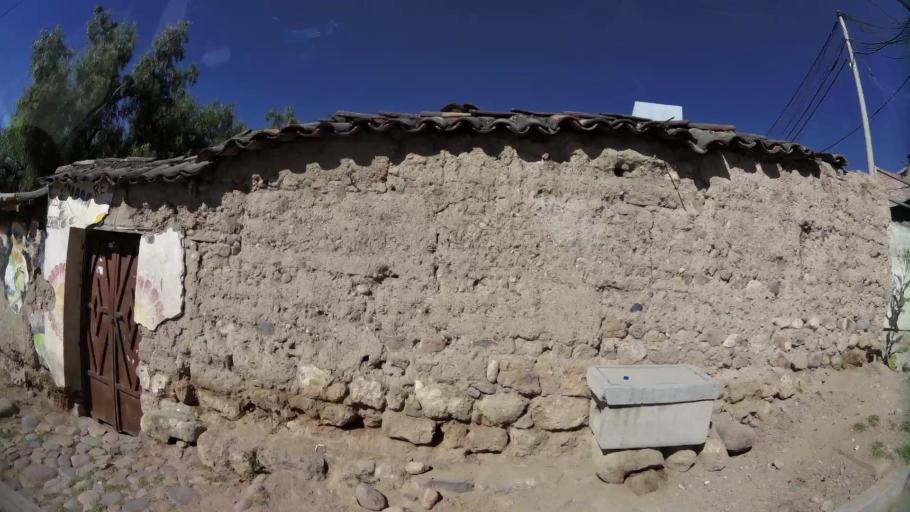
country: PE
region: Ayacucho
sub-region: Provincia de Huamanga
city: Ayacucho
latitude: -13.1643
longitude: -74.2314
